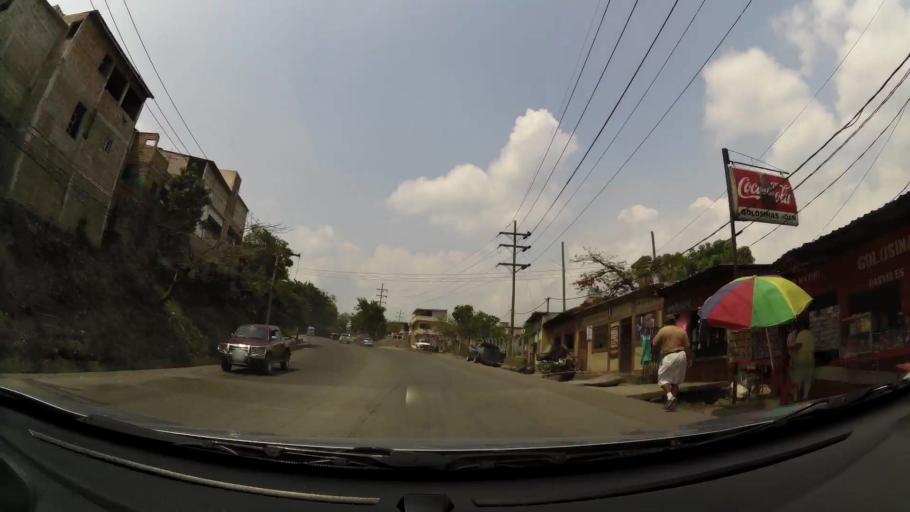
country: HN
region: Francisco Morazan
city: Tegucigalpa
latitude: 14.1064
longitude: -87.2317
